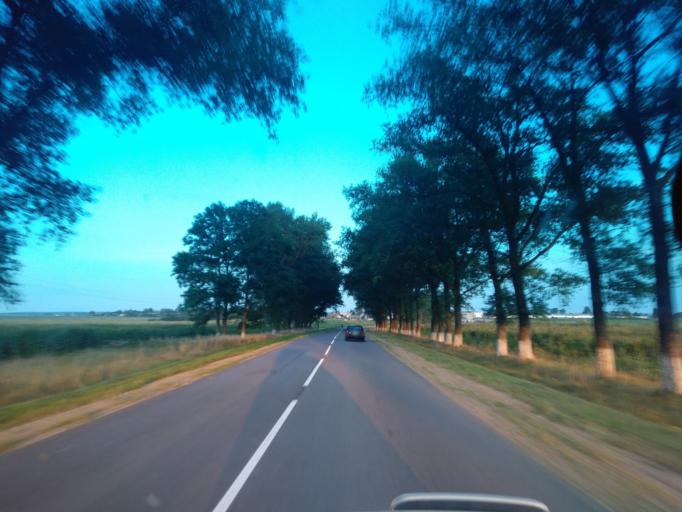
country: BY
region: Minsk
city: Slutsk
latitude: 53.1517
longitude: 27.5324
